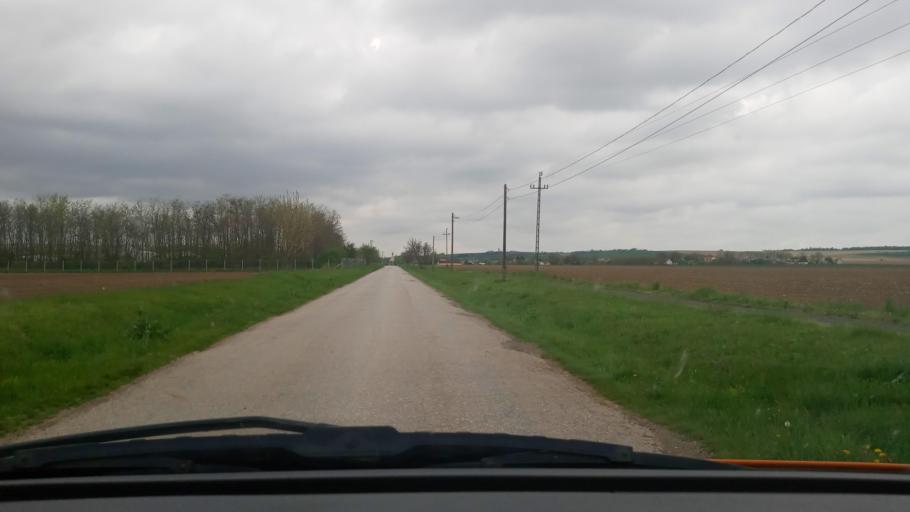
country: HU
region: Baranya
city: Boly
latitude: 45.9906
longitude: 18.5597
